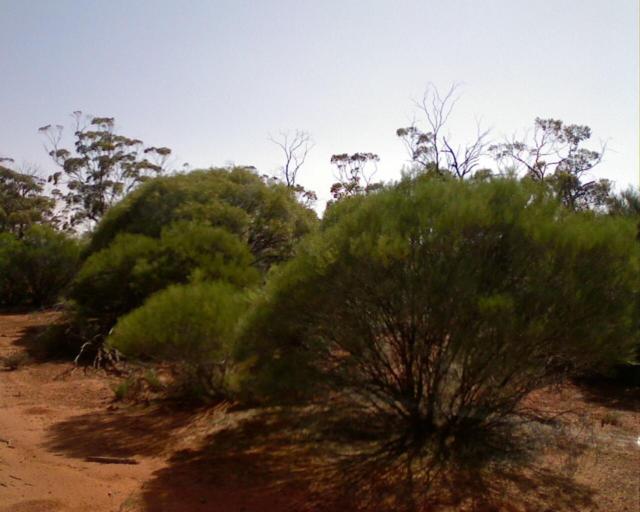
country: AU
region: Western Australia
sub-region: Merredin
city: Merredin
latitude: -30.9591
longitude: 118.8837
